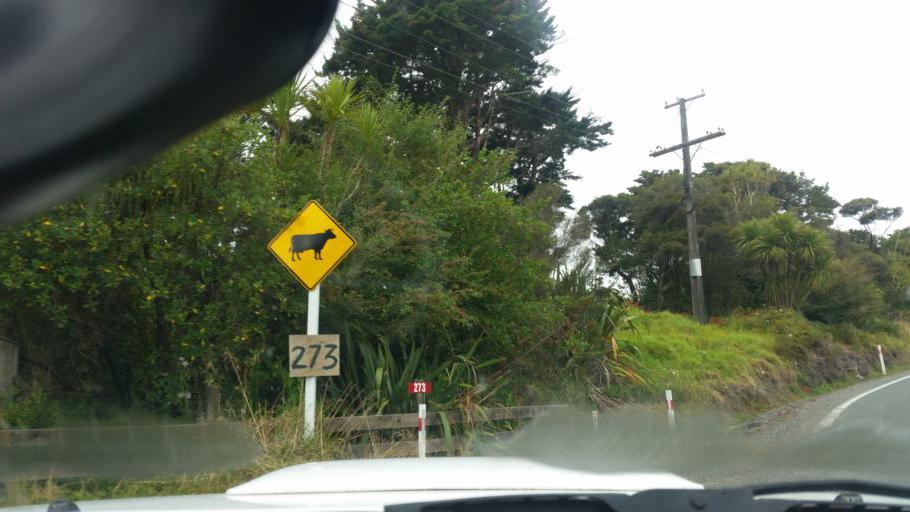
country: NZ
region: Auckland
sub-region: Auckland
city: Wellsford
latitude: -36.1521
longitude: 174.4691
